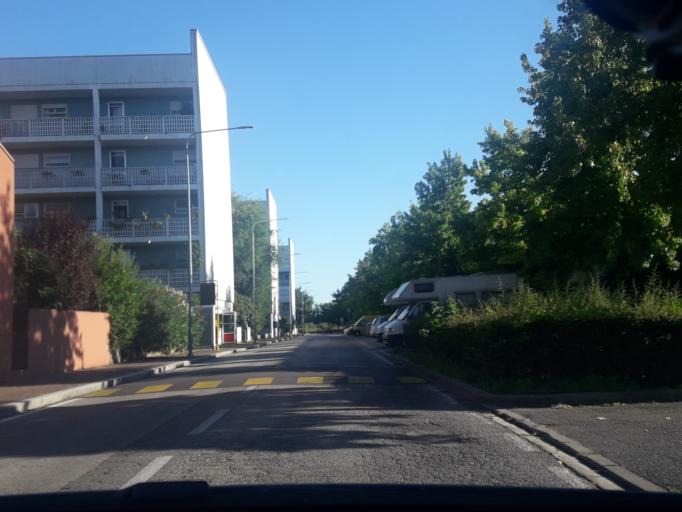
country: IT
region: Friuli Venezia Giulia
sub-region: Provincia di Udine
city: Passons
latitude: 46.0691
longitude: 13.2099
